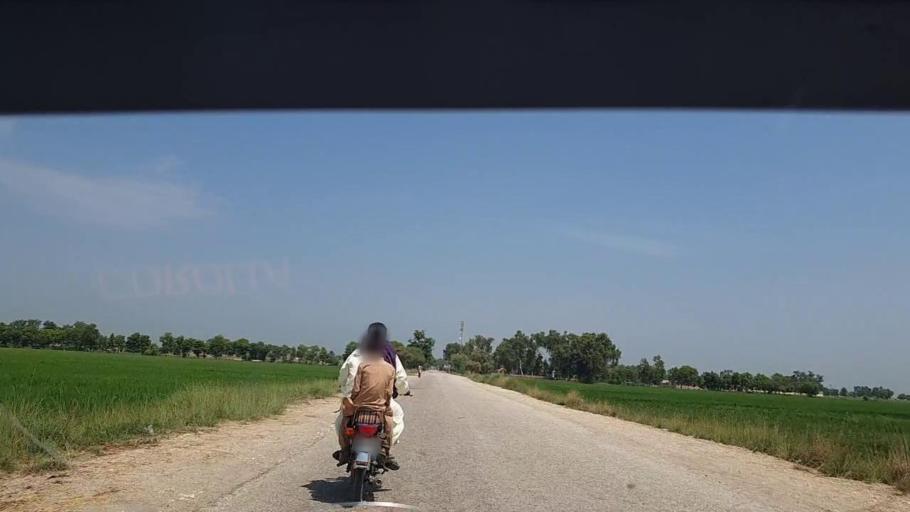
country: PK
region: Sindh
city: Rustam jo Goth
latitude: 28.0744
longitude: 68.7832
